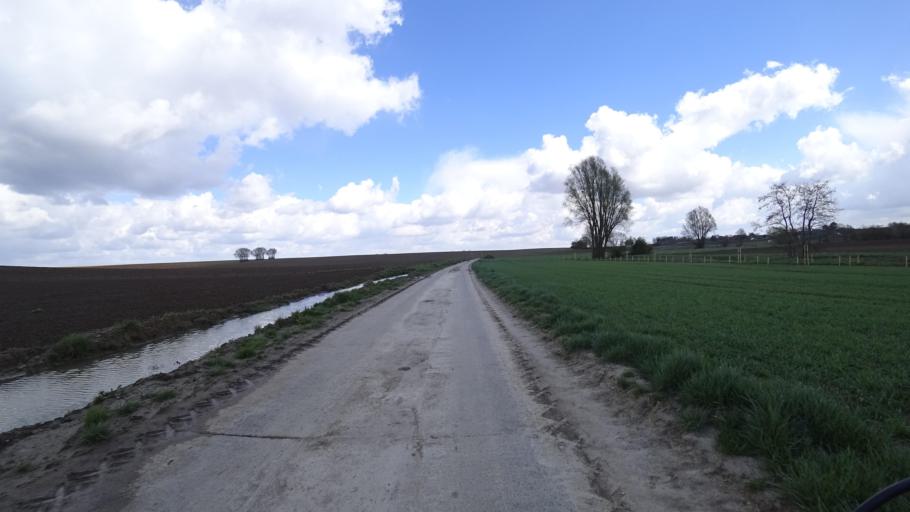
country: BE
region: Wallonia
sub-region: Province du Brabant Wallon
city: Walhain-Saint-Paul
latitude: 50.6532
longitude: 4.7058
